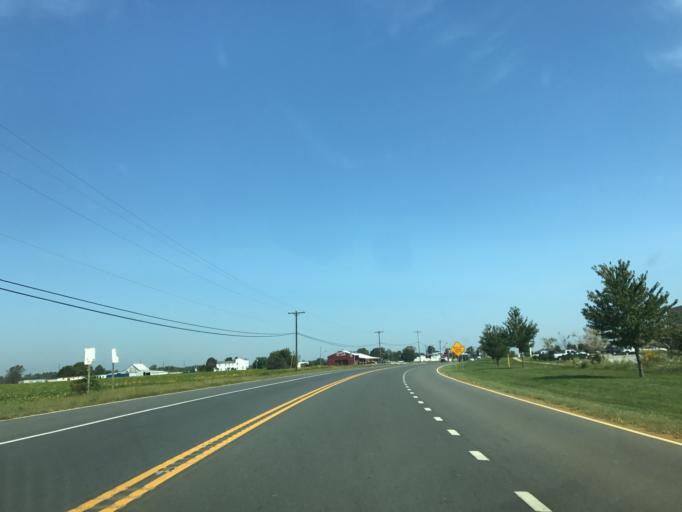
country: US
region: Delaware
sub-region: New Castle County
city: Middletown
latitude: 39.4349
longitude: -75.7575
